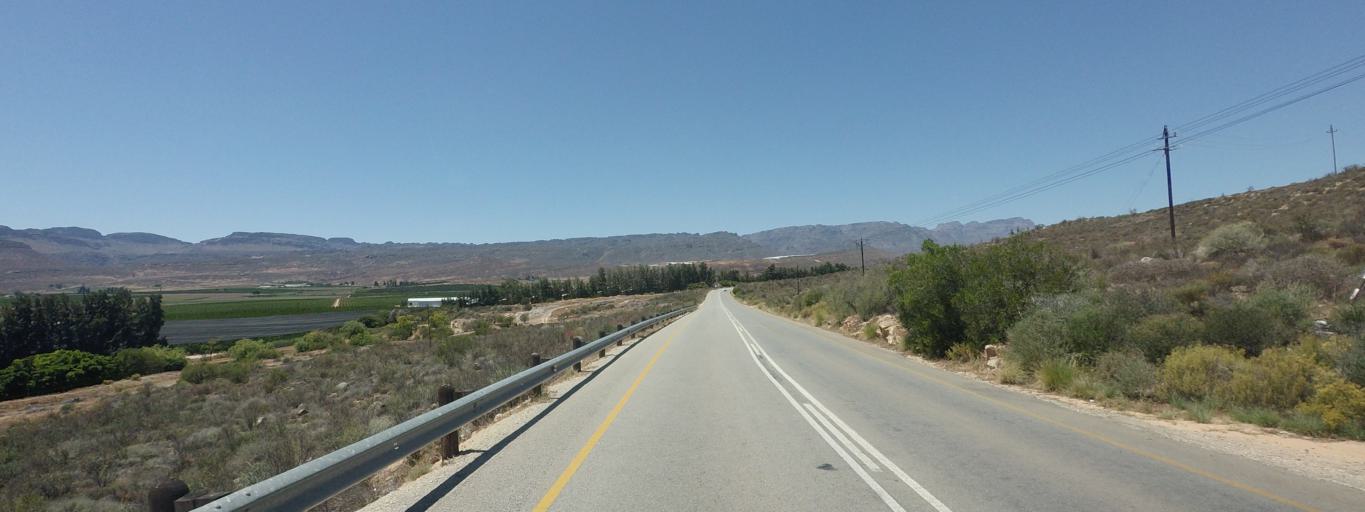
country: ZA
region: Western Cape
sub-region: West Coast District Municipality
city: Clanwilliam
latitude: -32.1702
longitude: 18.8753
